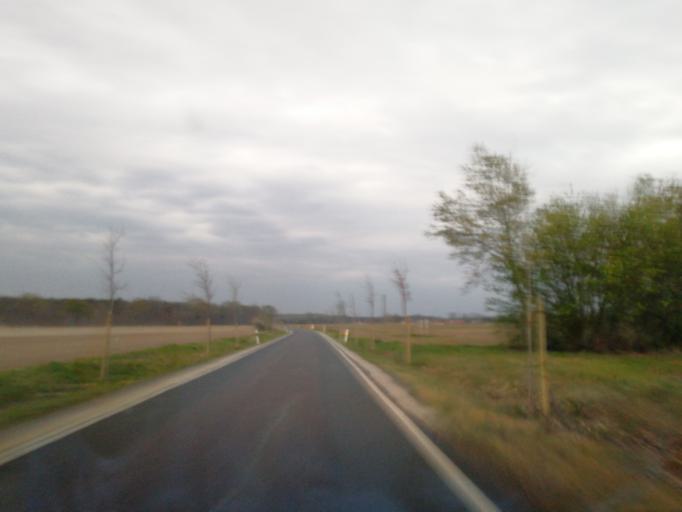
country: DE
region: Brandenburg
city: Calau
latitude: 51.7673
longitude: 13.8977
